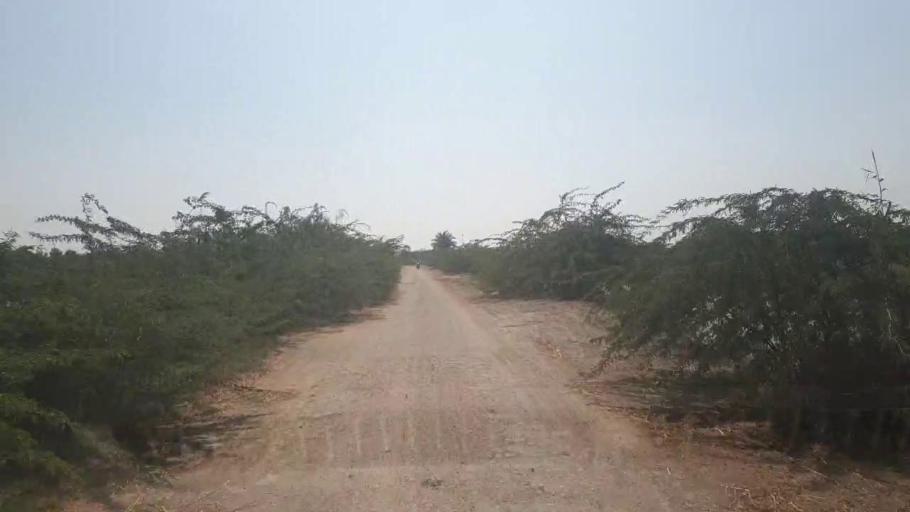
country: PK
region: Sindh
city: Badin
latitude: 24.6484
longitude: 68.9169
